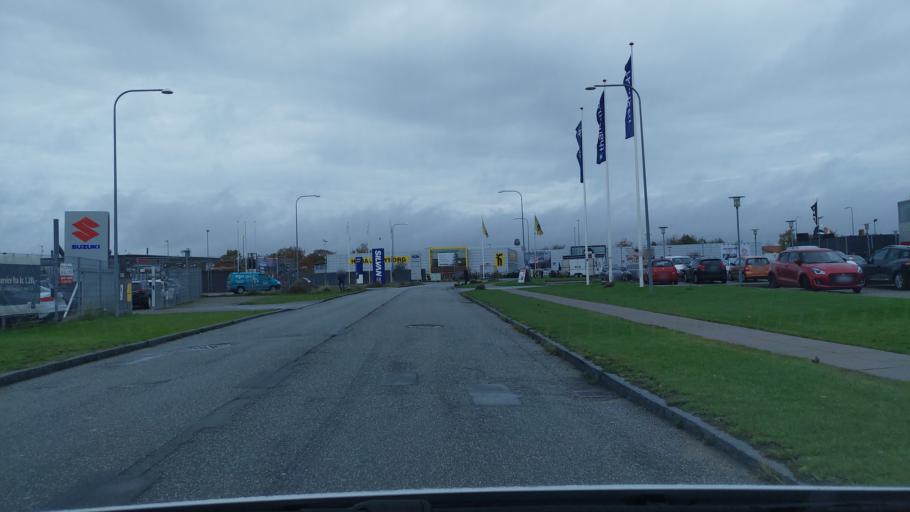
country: DK
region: Capital Region
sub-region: Tarnby Kommune
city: Tarnby
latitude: 55.6157
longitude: 12.6119
